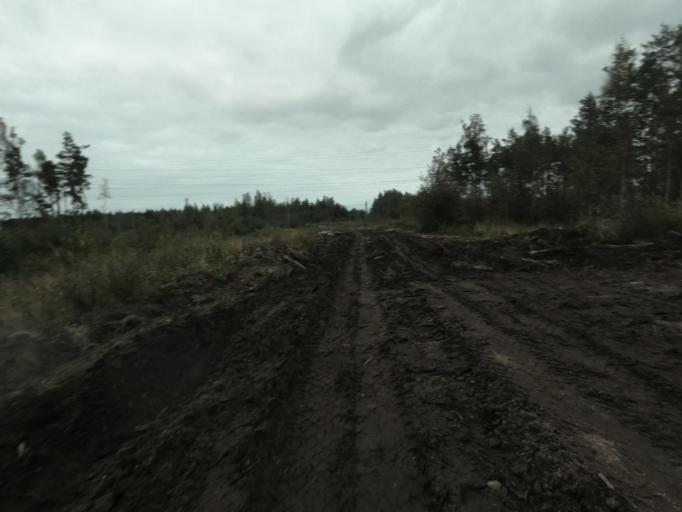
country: RU
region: St.-Petersburg
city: Sapernyy
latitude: 59.7641
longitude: 30.7244
